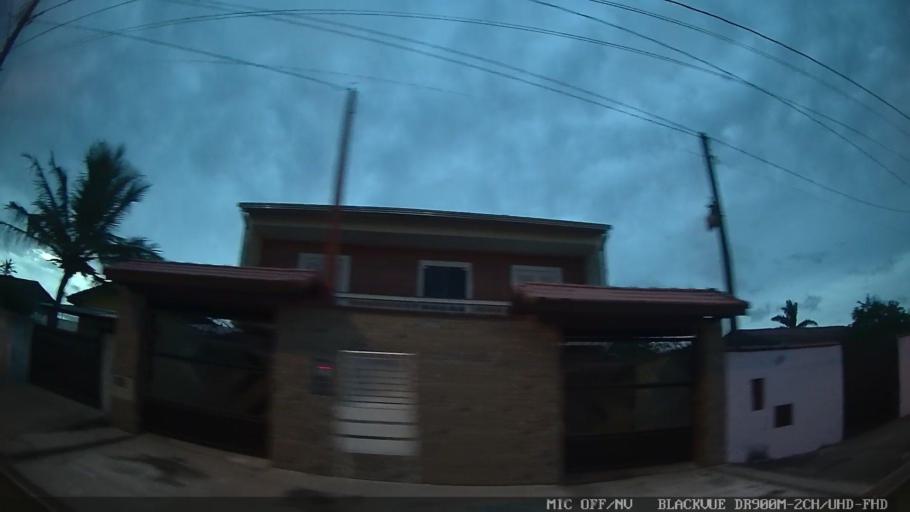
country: BR
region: Sao Paulo
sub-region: Iguape
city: Iguape
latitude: -24.7425
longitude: -47.5459
